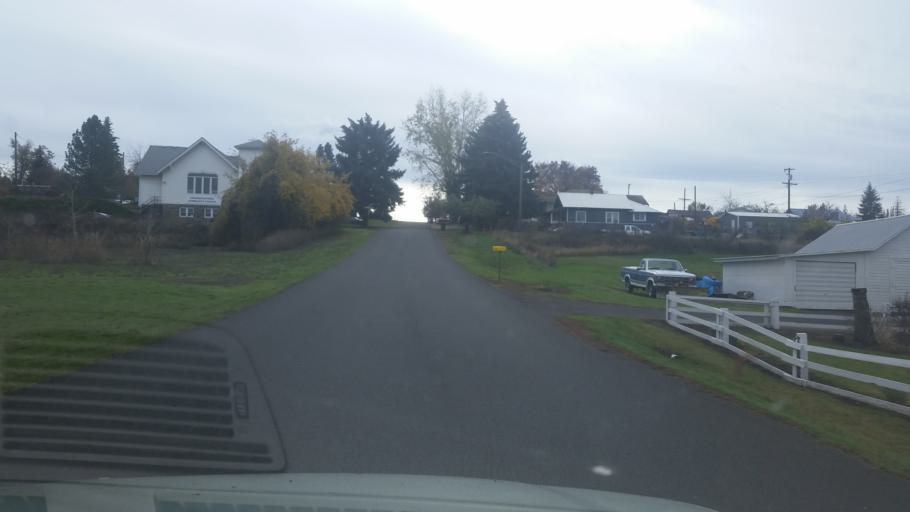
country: US
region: Washington
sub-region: Spokane County
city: Cheney
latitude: 47.2285
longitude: -117.4744
